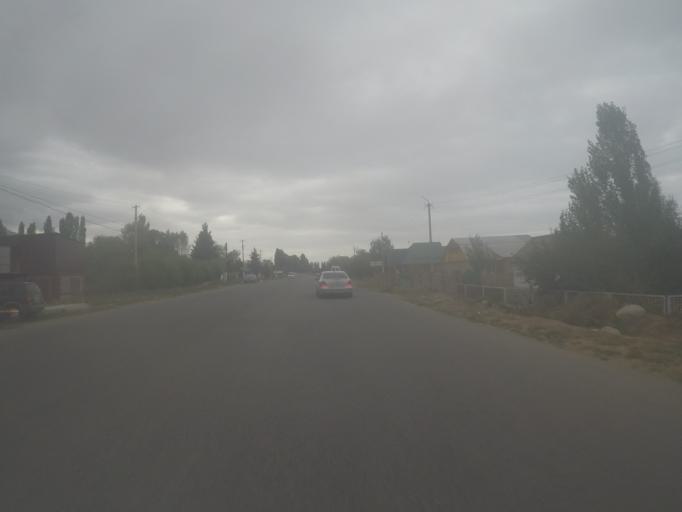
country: KG
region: Ysyk-Koel
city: Cholpon-Ata
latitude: 42.6909
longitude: 77.3663
